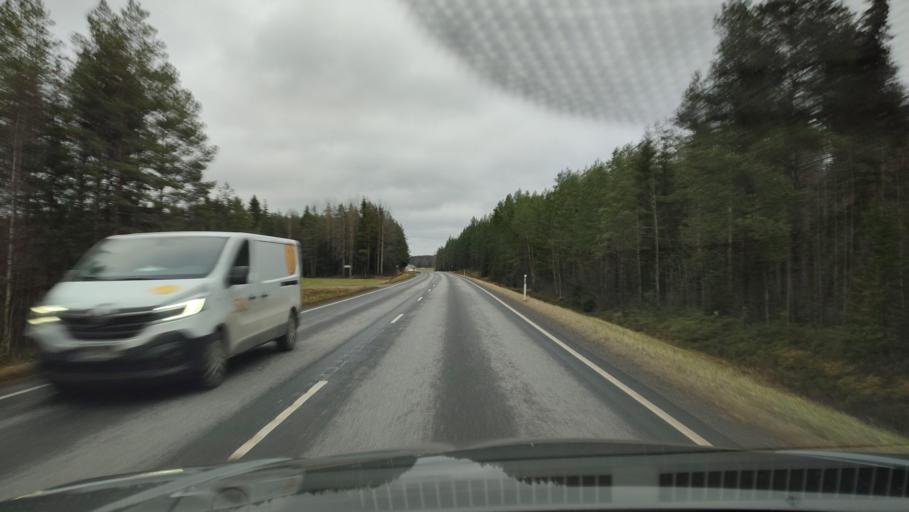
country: FI
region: Southern Ostrobothnia
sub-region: Suupohja
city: Kauhajoki
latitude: 62.4924
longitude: 22.2956
